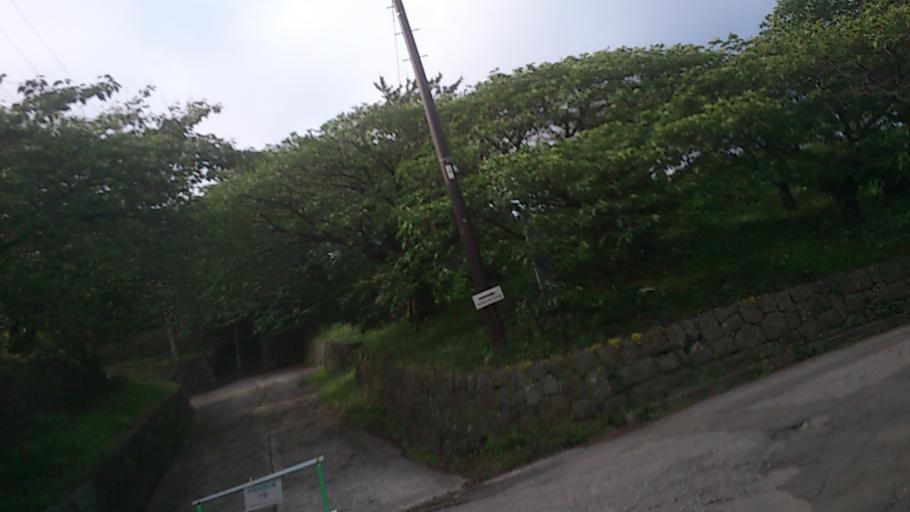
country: JP
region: Hokkaido
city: Kamiiso
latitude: 41.4288
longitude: 140.1082
